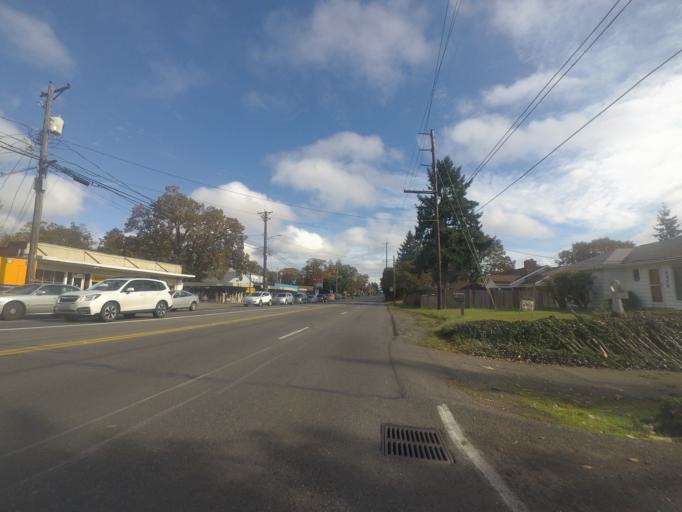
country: US
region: Washington
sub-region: Pierce County
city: Lakewood
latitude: 47.1764
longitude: -122.5176
